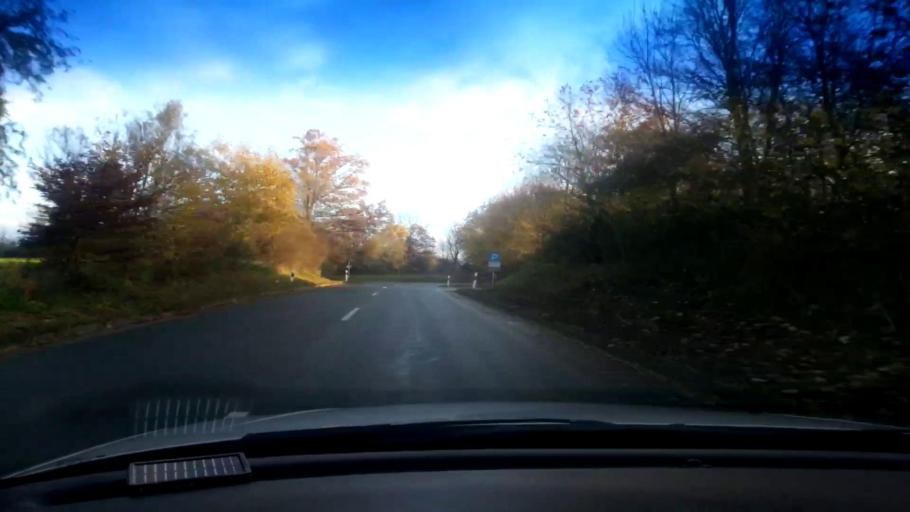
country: DE
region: Bavaria
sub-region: Upper Franconia
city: Strullendorf
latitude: 49.8665
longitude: 11.0010
